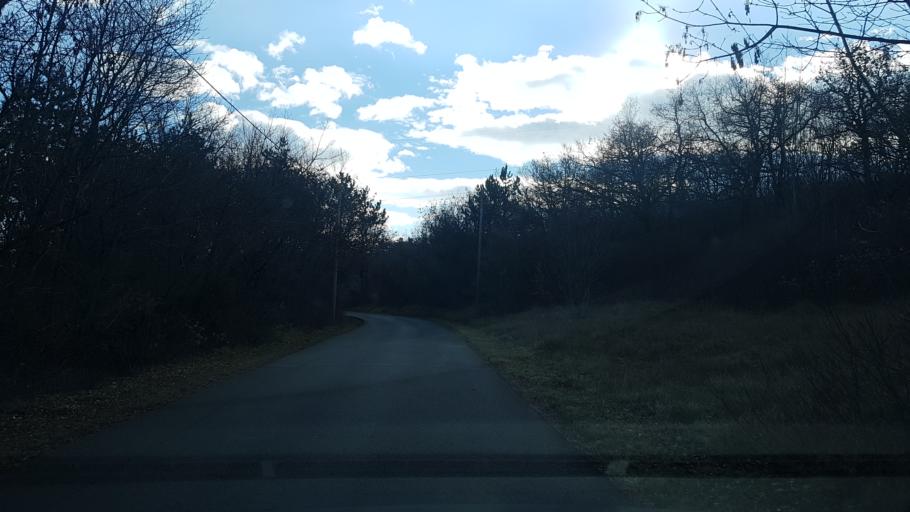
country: IT
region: Friuli Venezia Giulia
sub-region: Provincia di Gorizia
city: Gradisca d'Isonzo
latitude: 45.8798
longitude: 13.5242
